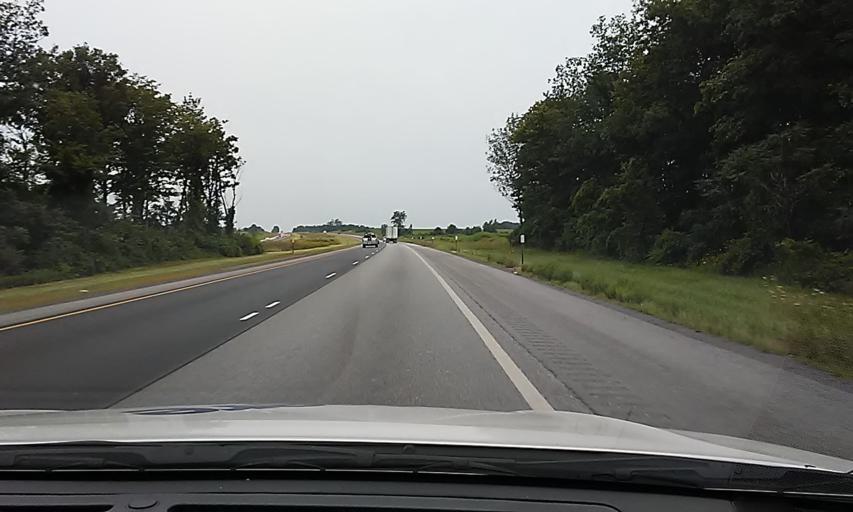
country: US
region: New York
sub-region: Genesee County
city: Le Roy
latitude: 43.0300
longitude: -78.0390
